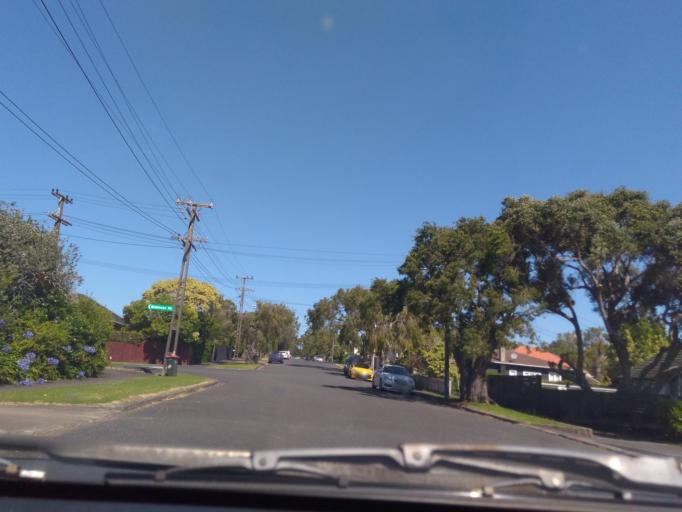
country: NZ
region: Auckland
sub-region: Auckland
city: Rosebank
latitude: -36.8801
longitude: 174.6980
